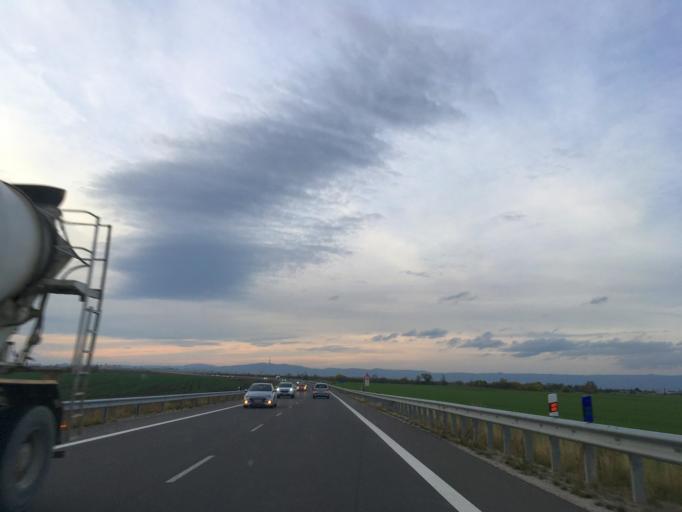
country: SK
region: Bratislavsky
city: Dunajska Luzna
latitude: 48.1299
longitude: 17.2650
